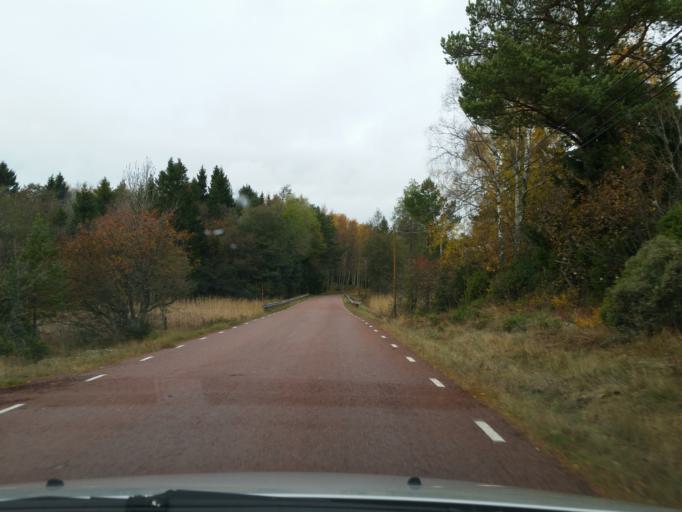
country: AX
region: Alands landsbygd
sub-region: Lemland
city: Lemland
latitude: 60.0126
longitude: 20.1835
